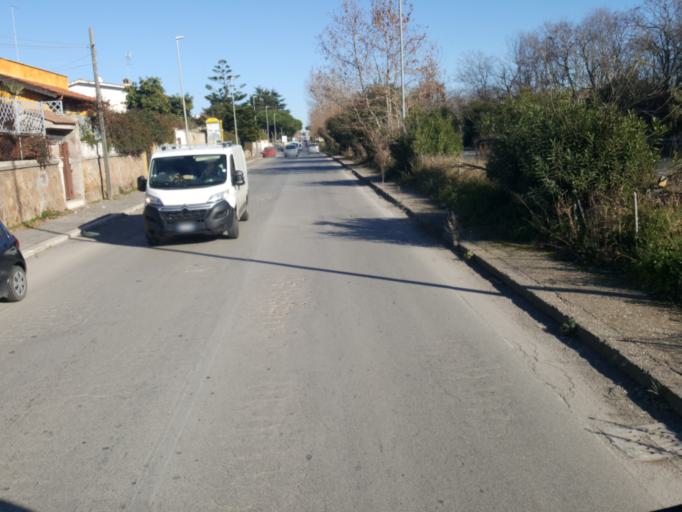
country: IT
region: Latium
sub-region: Citta metropolitana di Roma Capitale
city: Acilia-Castel Fusano-Ostia Antica
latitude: 41.7786
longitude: 12.3476
